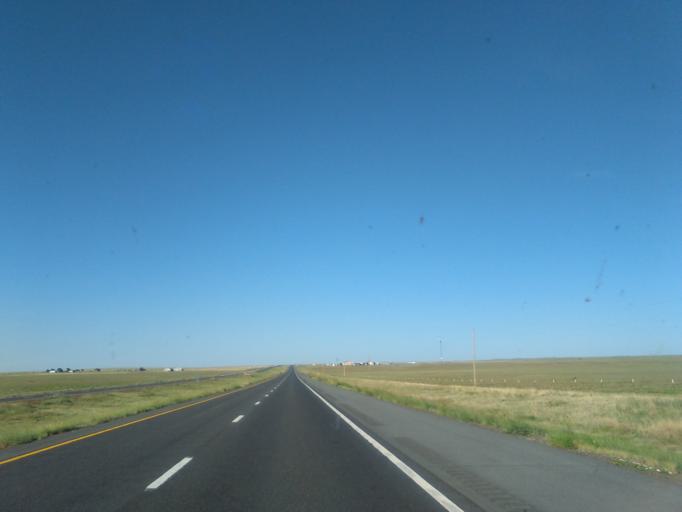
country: US
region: New Mexico
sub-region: San Miguel County
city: Las Vegas
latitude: 35.6888
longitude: -105.1361
